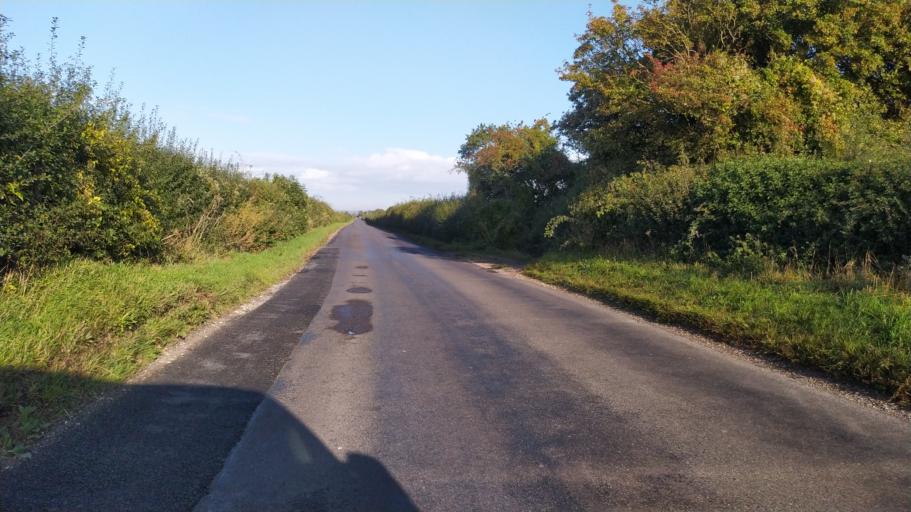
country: GB
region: England
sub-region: Dorset
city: Wimborne Minster
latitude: 50.8929
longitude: -2.0129
